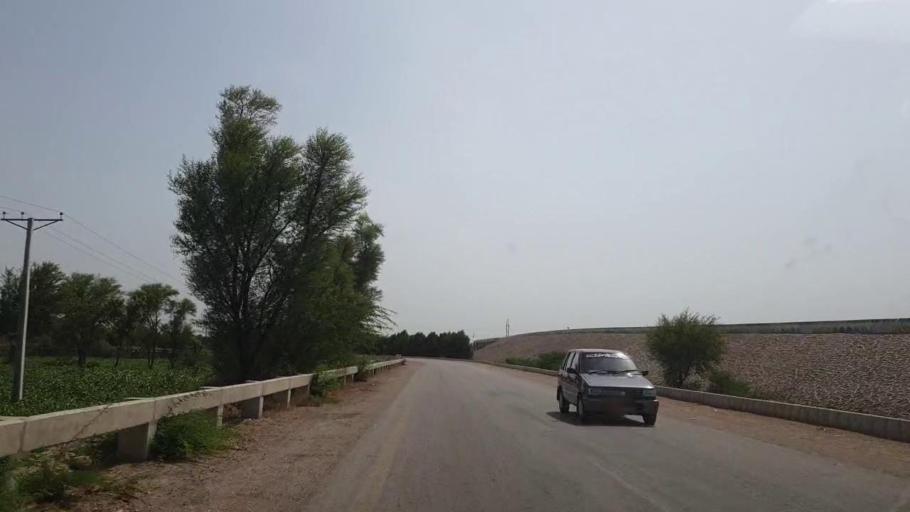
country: PK
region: Sindh
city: Sakrand
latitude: 26.1568
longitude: 68.2525
